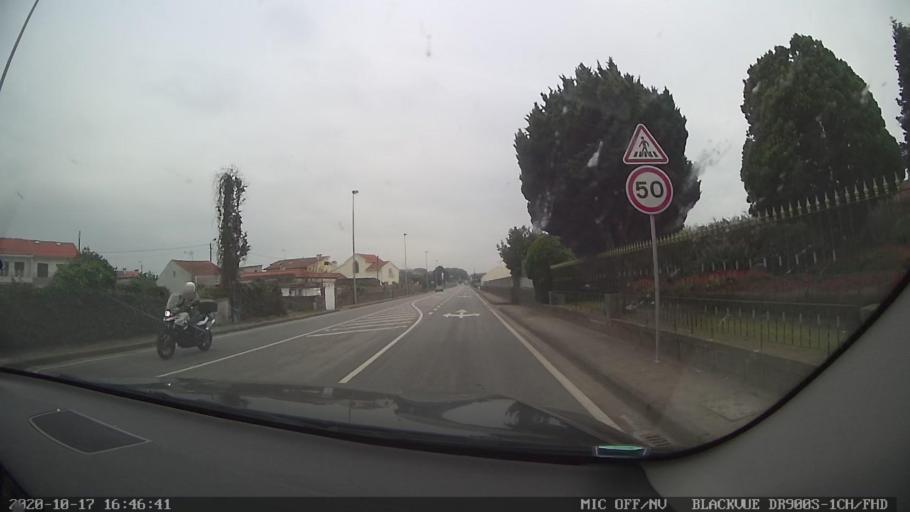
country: PT
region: Braga
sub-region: Esposende
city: Esposende
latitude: 41.5360
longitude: -8.7791
